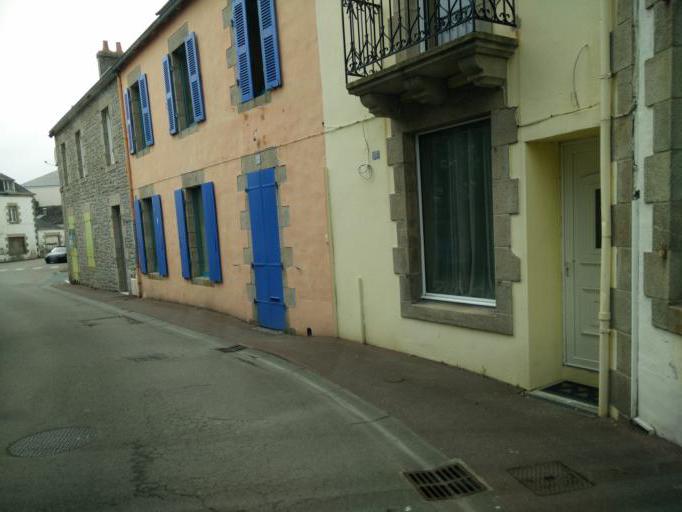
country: FR
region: Brittany
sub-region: Departement du Finistere
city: Plobannalec-Lesconil
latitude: 47.7981
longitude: -4.2146
